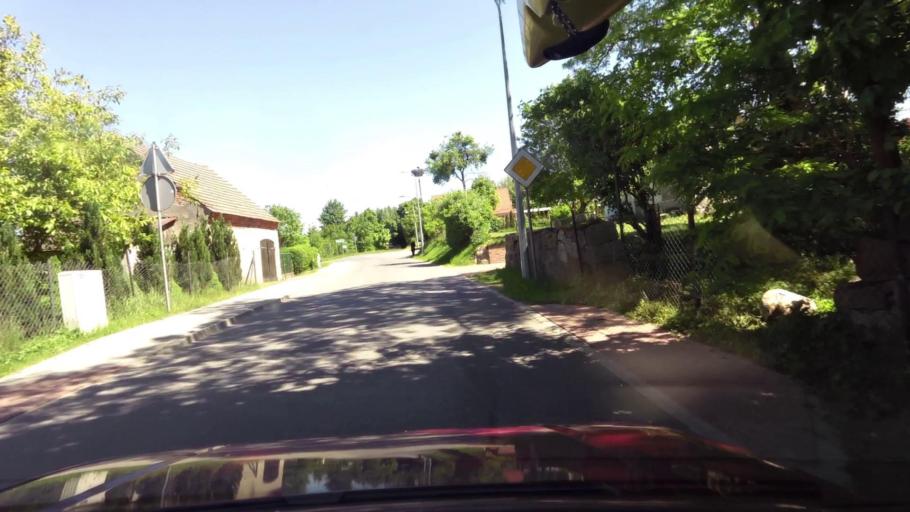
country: PL
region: West Pomeranian Voivodeship
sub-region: Powiat koszalinski
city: Polanow
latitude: 54.0434
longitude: 16.7238
